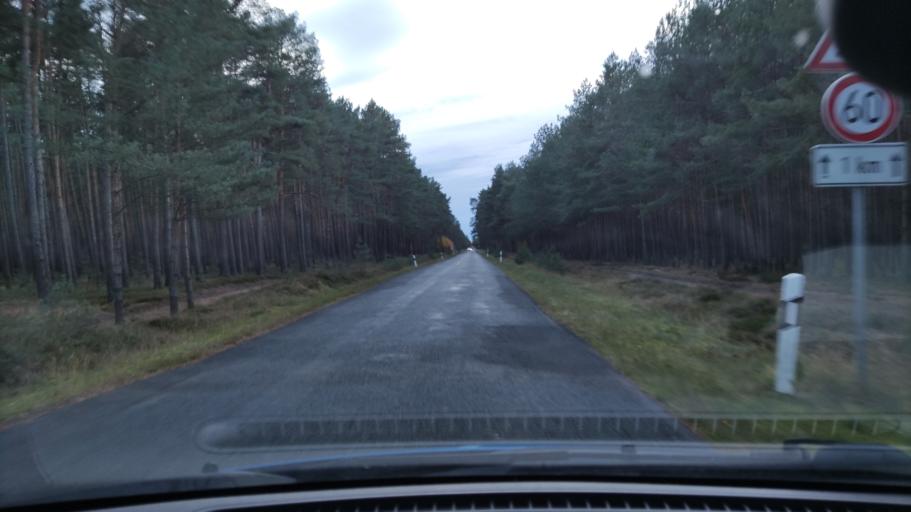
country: DE
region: Saxony-Anhalt
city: Luftkurort Arendsee
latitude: 52.9353
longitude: 11.5120
